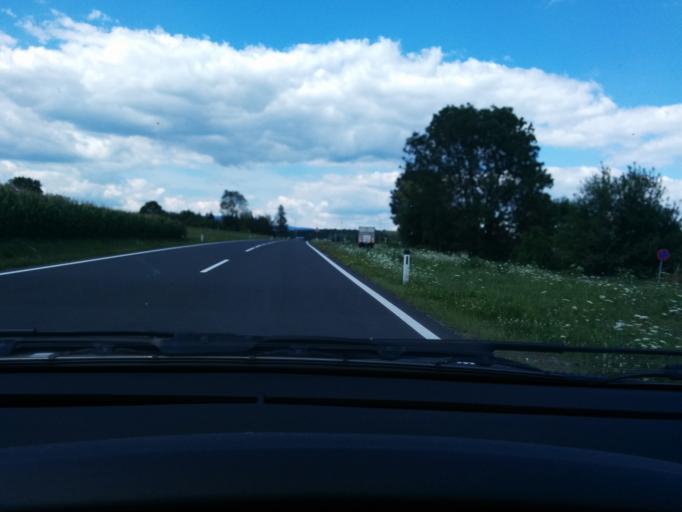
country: AT
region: Styria
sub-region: Politischer Bezirk Hartberg-Fuerstenfeld
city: Hartberg
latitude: 47.2955
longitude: 15.9799
